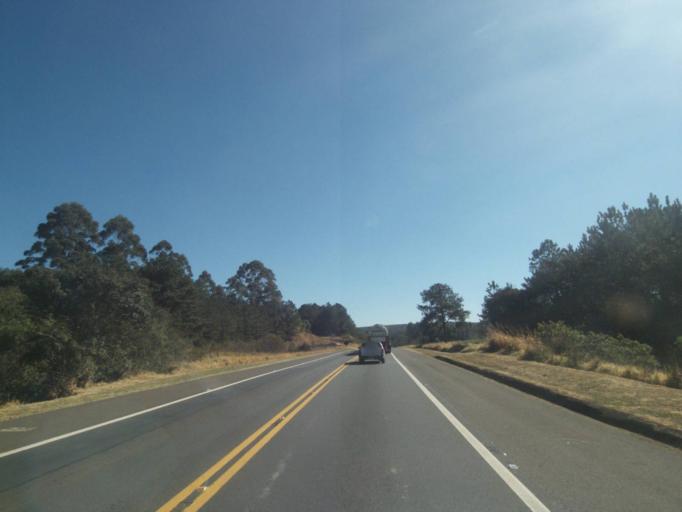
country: BR
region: Parana
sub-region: Tibagi
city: Tibagi
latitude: -24.7023
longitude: -50.5731
